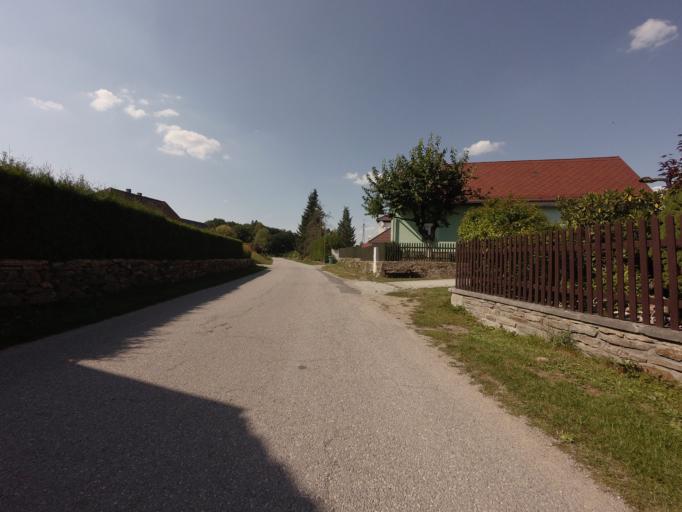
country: CZ
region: Jihocesky
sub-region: Okres Ceske Budejovice
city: Hluboka nad Vltavou
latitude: 49.1310
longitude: 14.4518
